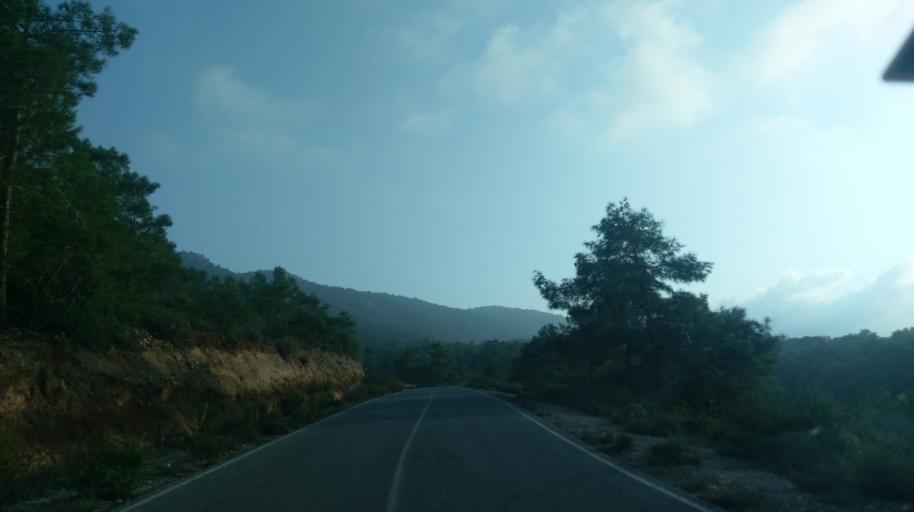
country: CY
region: Ammochostos
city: Trikomo
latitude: 35.4128
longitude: 33.9037
